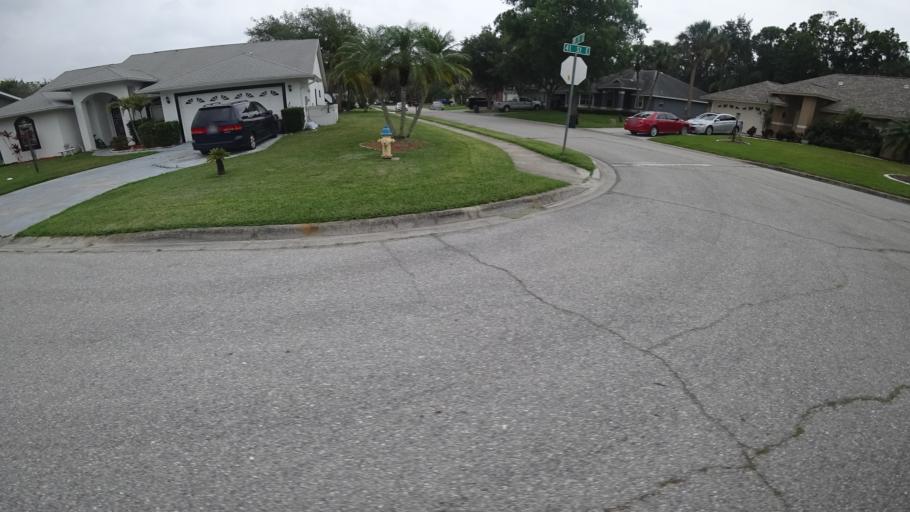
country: US
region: Florida
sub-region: Manatee County
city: Samoset
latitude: 27.4368
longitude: -82.5113
